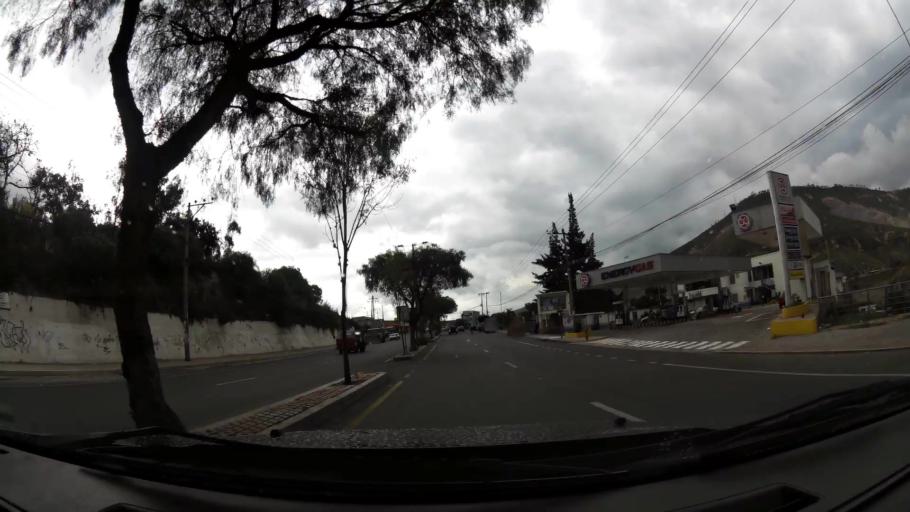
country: EC
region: Pichincha
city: Quito
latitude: -0.0577
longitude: -78.4554
